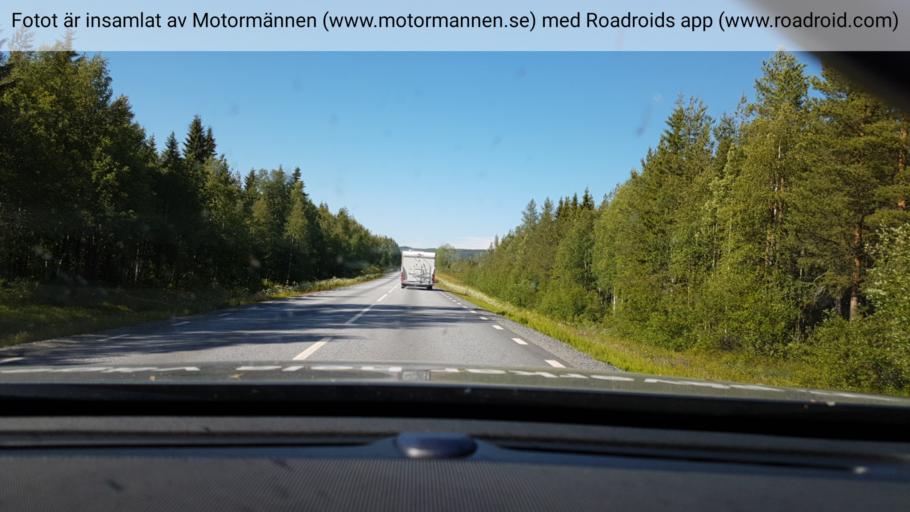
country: SE
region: Vaesterbotten
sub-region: Vilhelmina Kommun
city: Vilhelmina
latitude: 64.5743
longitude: 16.7442
